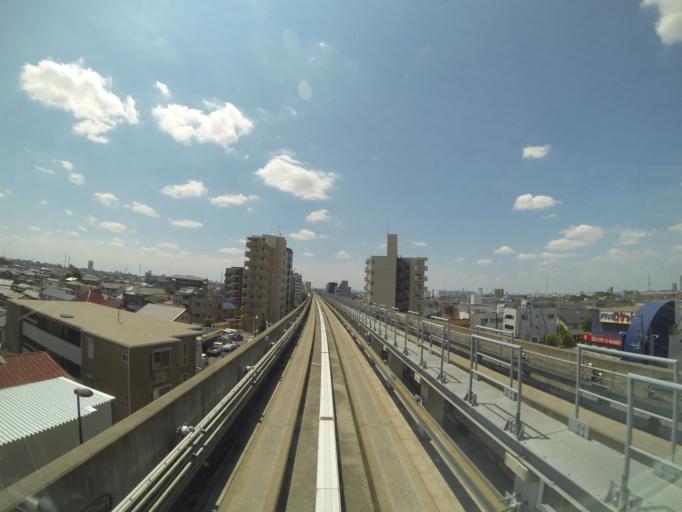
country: JP
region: Saitama
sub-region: Kawaguchi-shi
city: Hatogaya-honcho
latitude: 35.8110
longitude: 139.7701
